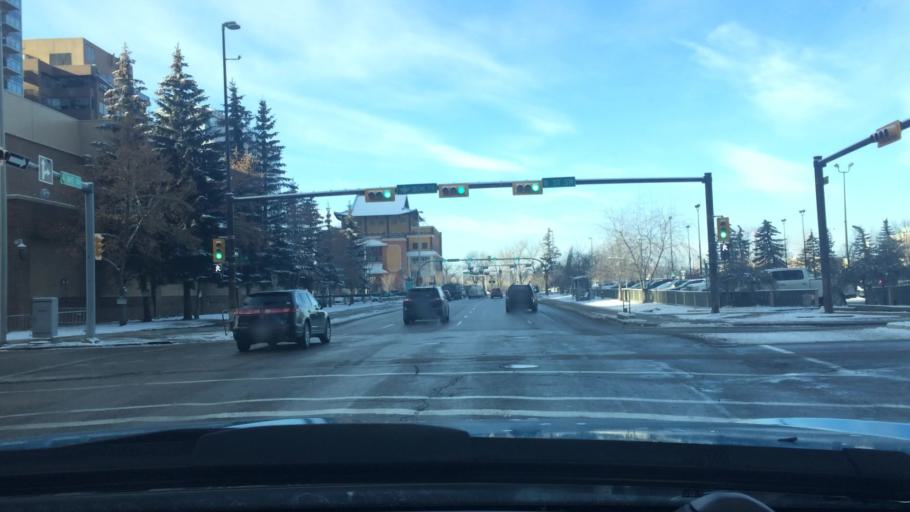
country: CA
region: Alberta
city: Calgary
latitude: 51.0499
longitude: -114.0807
